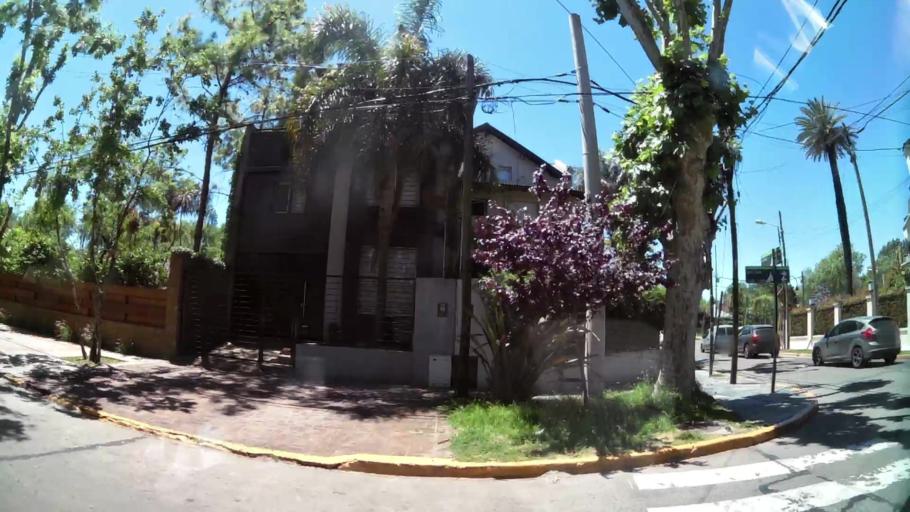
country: AR
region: Buenos Aires
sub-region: Partido de Tigre
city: Tigre
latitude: -34.4441
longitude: -58.5432
